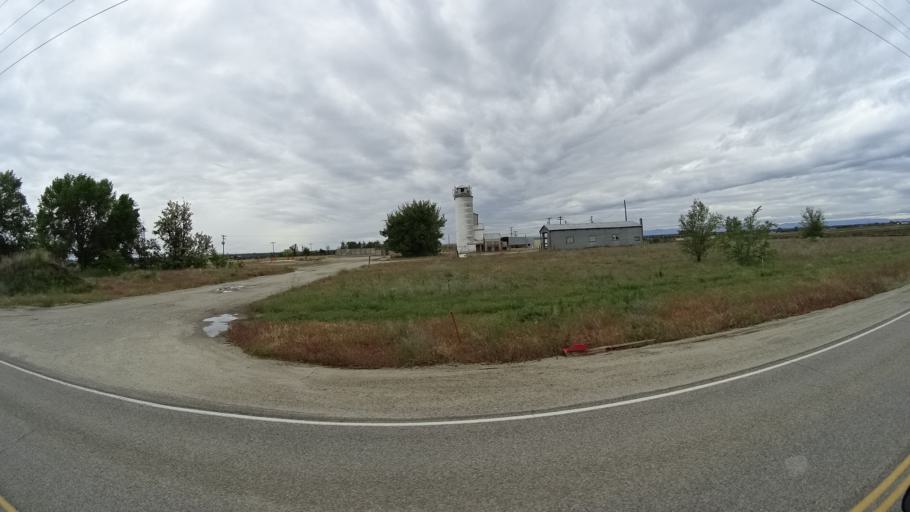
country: US
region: Idaho
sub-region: Ada County
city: Star
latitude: 43.7213
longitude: -116.4342
